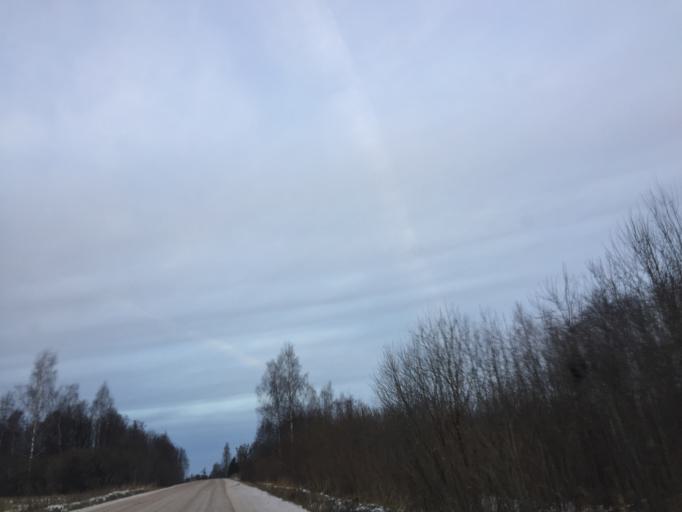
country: LV
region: Limbazu Rajons
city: Limbazi
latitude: 57.5779
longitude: 24.8285
